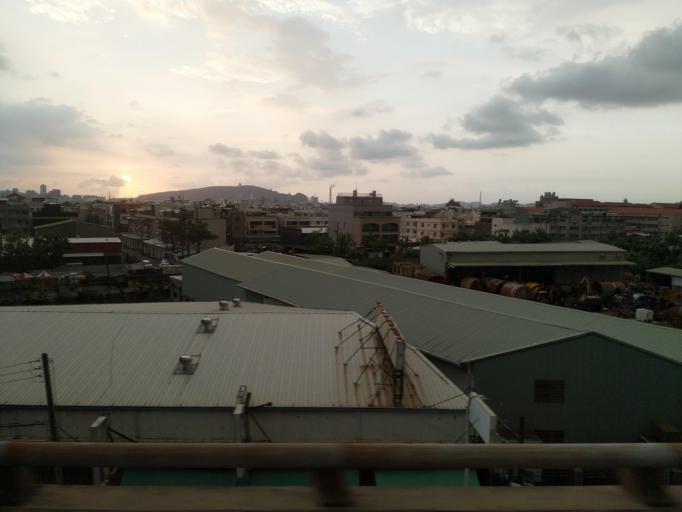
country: TW
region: Taiwan
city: Fengshan
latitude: 22.7001
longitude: 120.3592
